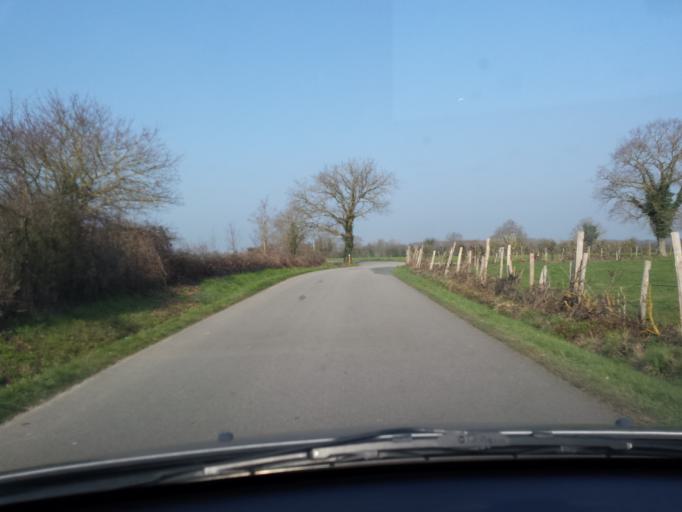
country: FR
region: Pays de la Loire
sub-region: Departement de la Vendee
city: Dompierre-sur-Yon
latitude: 46.7043
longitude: -1.3745
